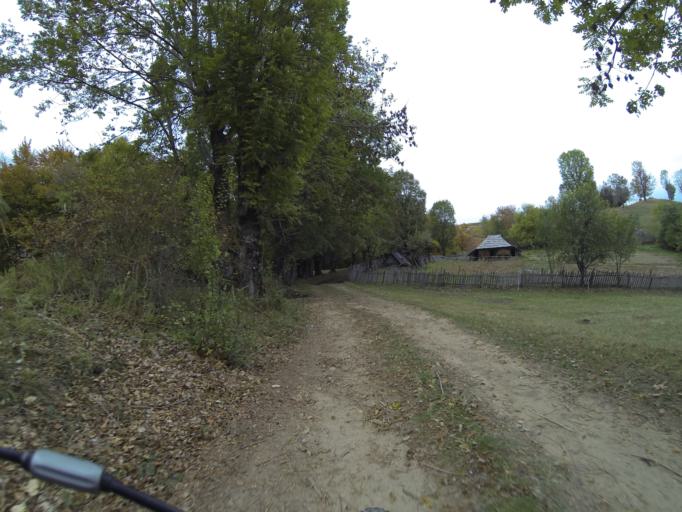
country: RO
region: Gorj
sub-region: Comuna Pades
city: Closani
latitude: 45.1092
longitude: 22.8459
